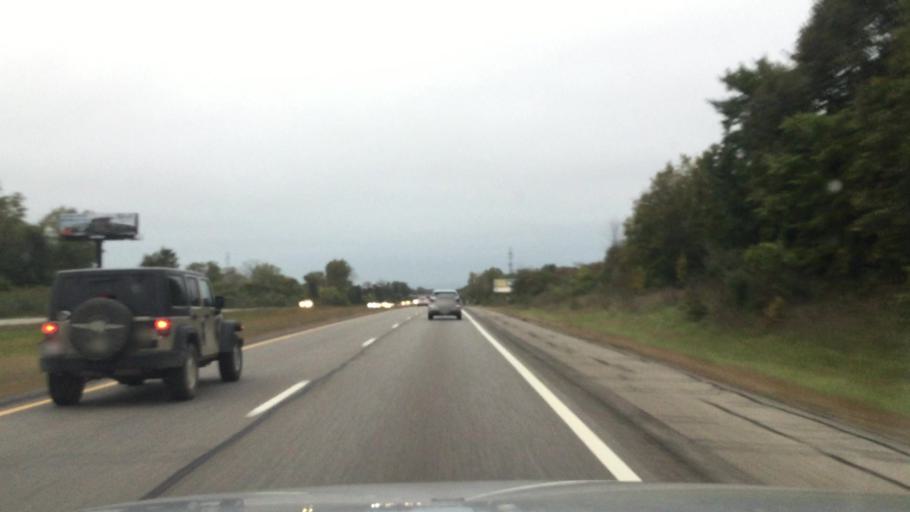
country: US
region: Michigan
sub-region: Genesee County
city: Grand Blanc
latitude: 42.9363
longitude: -83.7021
